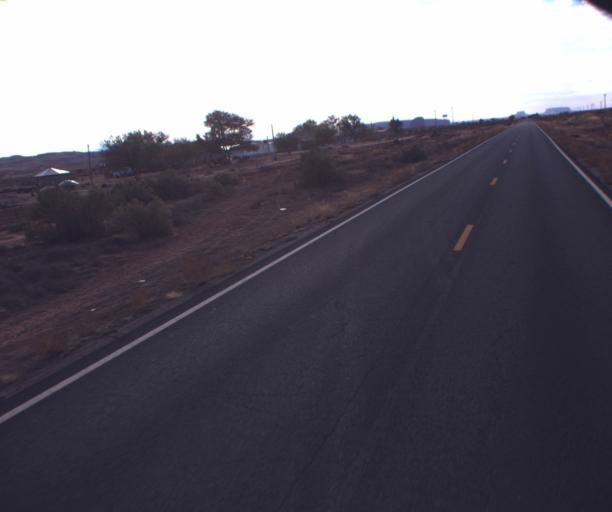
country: US
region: Arizona
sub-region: Apache County
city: Many Farms
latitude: 36.7334
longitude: -109.6330
